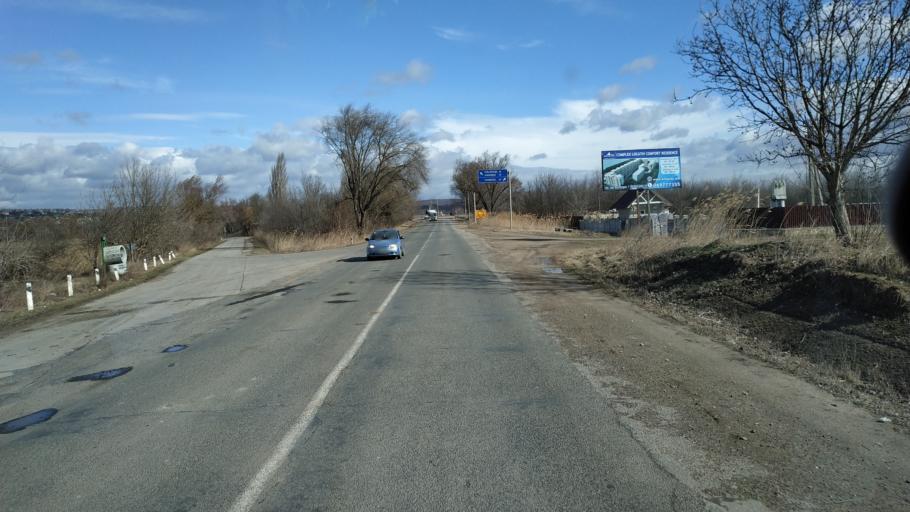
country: MD
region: Stinga Nistrului
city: Bucovat
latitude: 47.1784
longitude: 28.4636
